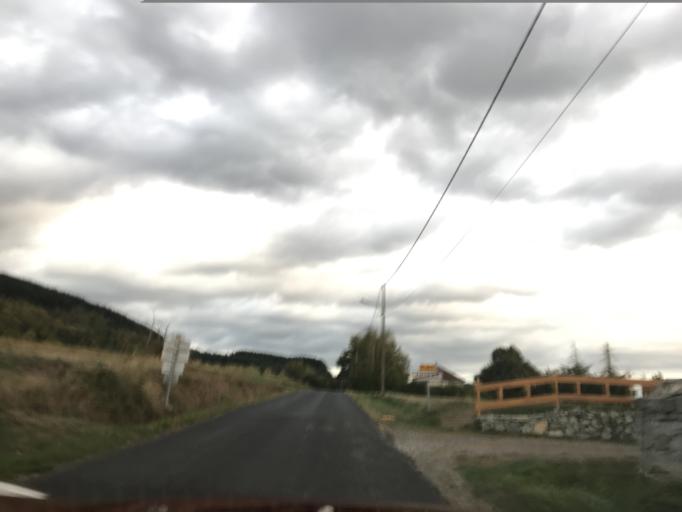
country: FR
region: Auvergne
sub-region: Departement du Puy-de-Dome
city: Thiers
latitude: 45.8372
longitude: 3.5468
